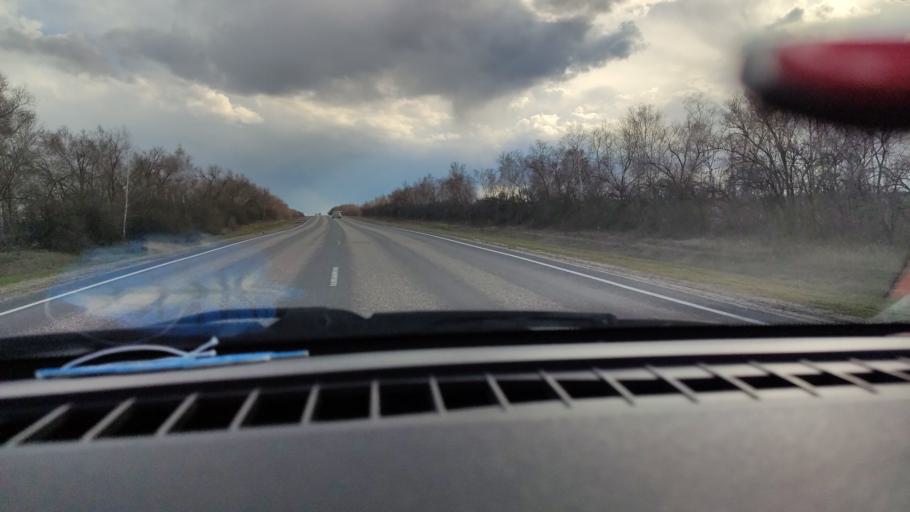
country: RU
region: Saratov
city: Sinodskoye
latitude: 51.9494
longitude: 46.6067
